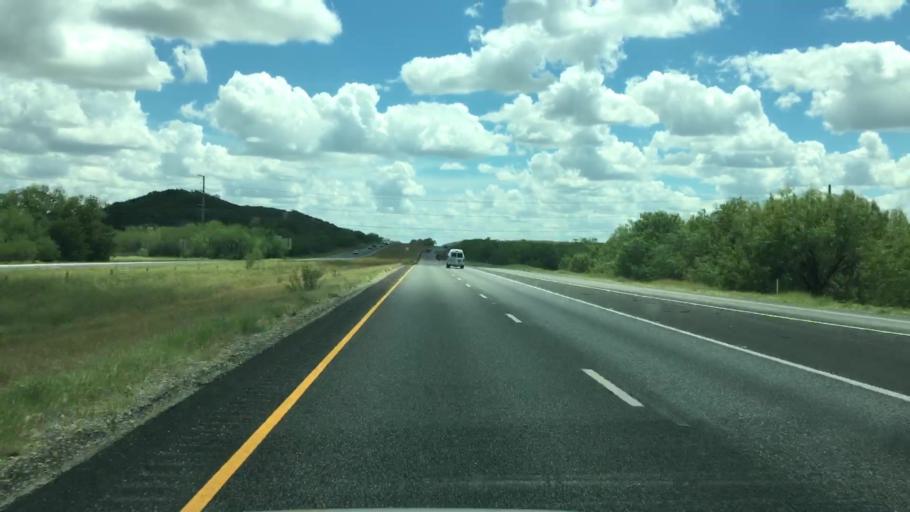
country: US
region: Texas
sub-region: Live Oak County
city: Three Rivers
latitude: 28.7281
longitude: -98.2877
